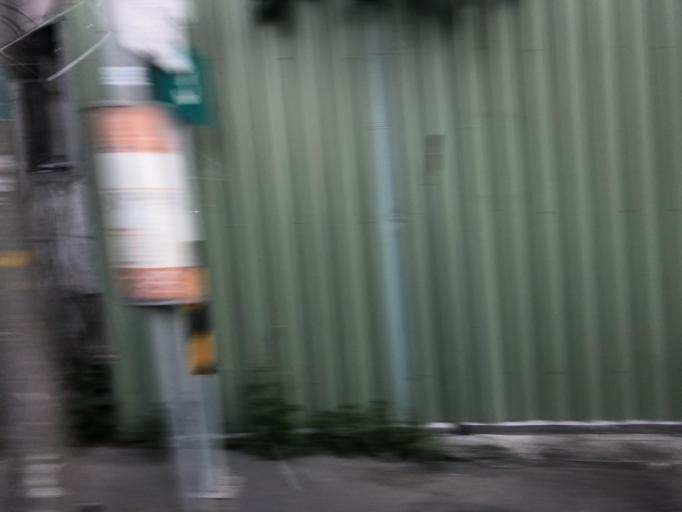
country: TW
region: Taiwan
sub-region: Tainan
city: Tainan
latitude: 23.1429
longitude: 120.2684
